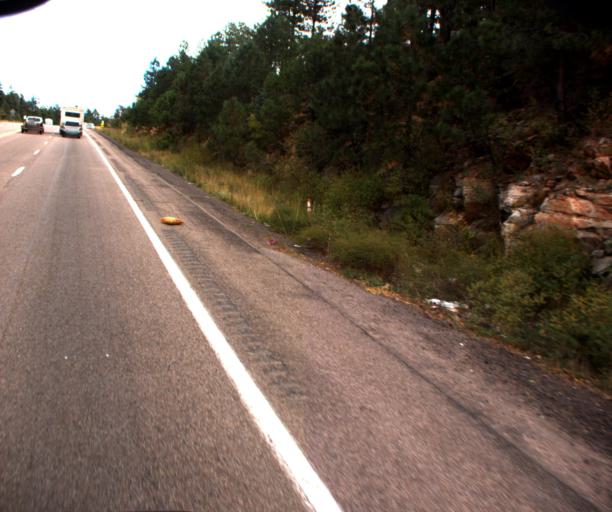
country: US
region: Arizona
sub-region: Navajo County
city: Heber-Overgaard
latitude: 34.3006
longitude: -110.9032
